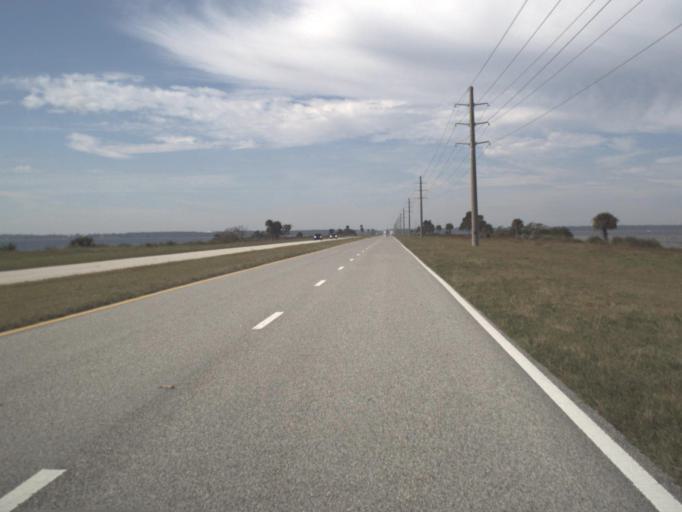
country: US
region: Florida
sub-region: Brevard County
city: Merritt Island
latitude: 28.5267
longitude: -80.7360
